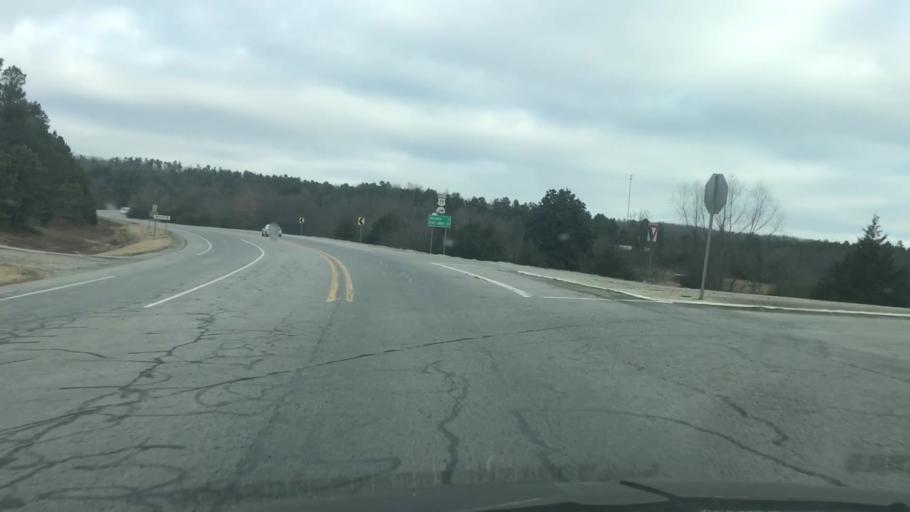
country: US
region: Arkansas
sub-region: Scott County
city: Waldron
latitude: 34.8085
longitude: -94.0394
